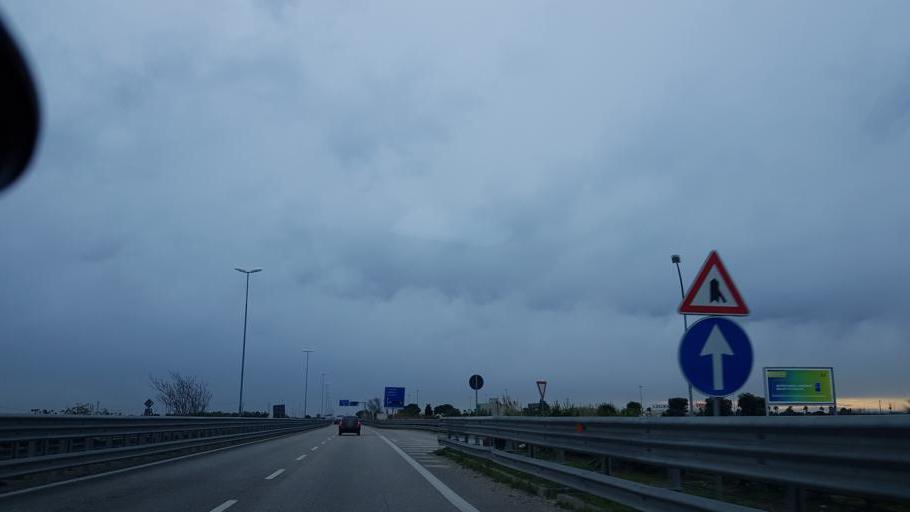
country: IT
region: Apulia
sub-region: Provincia di Brindisi
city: Brindisi
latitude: 40.6209
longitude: 17.9105
